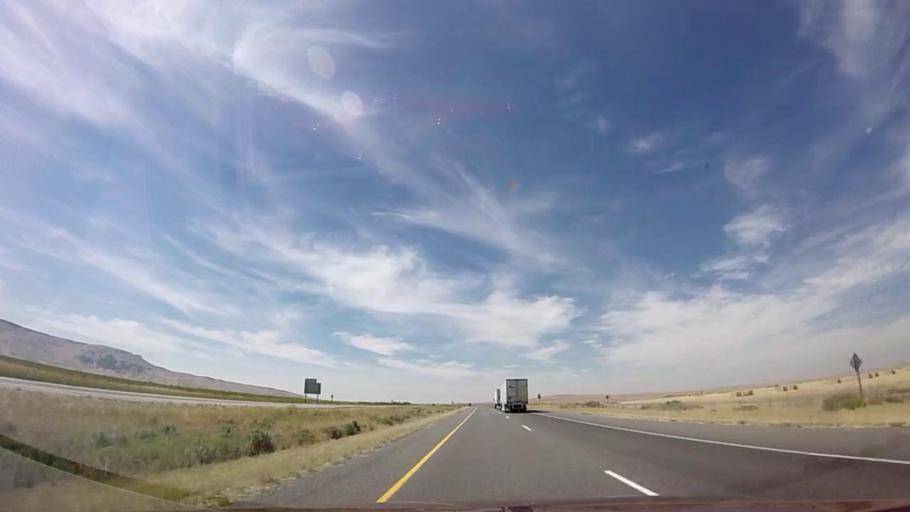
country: US
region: Idaho
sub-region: Minidoka County
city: Rupert
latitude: 42.5179
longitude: -113.4254
